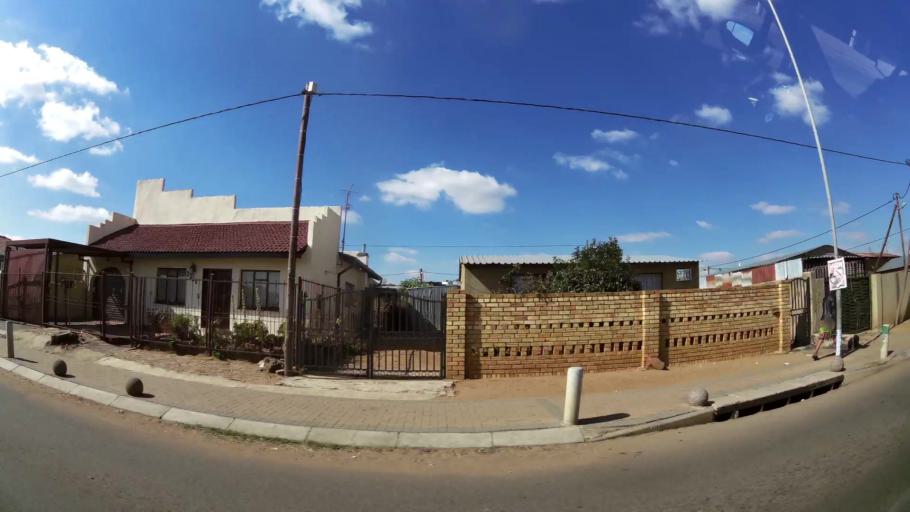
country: ZA
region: Gauteng
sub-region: West Rand District Municipality
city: Krugersdorp
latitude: -26.1562
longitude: 27.7845
